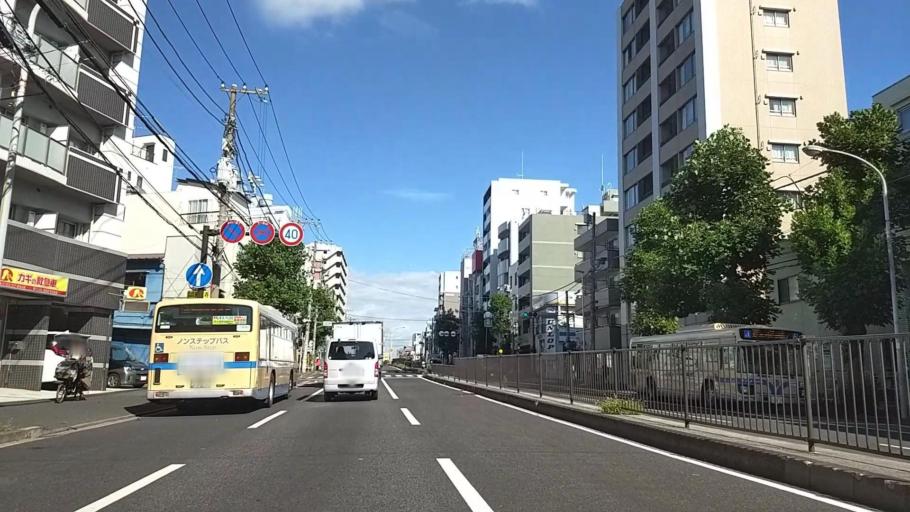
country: JP
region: Kanagawa
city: Yokohama
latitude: 35.4844
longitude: 139.6280
